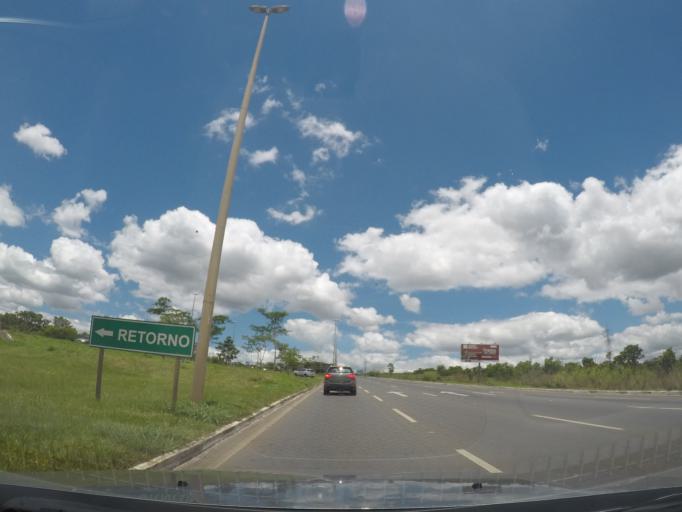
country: BR
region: Federal District
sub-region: Brasilia
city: Brasilia
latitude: -15.7226
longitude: -47.9058
